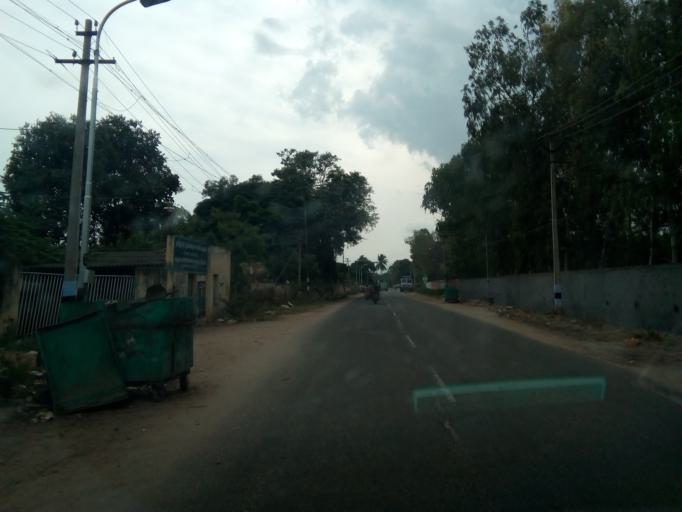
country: IN
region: Tamil Nadu
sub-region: Coimbatore
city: Coimbatore
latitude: 11.0060
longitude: 76.9384
